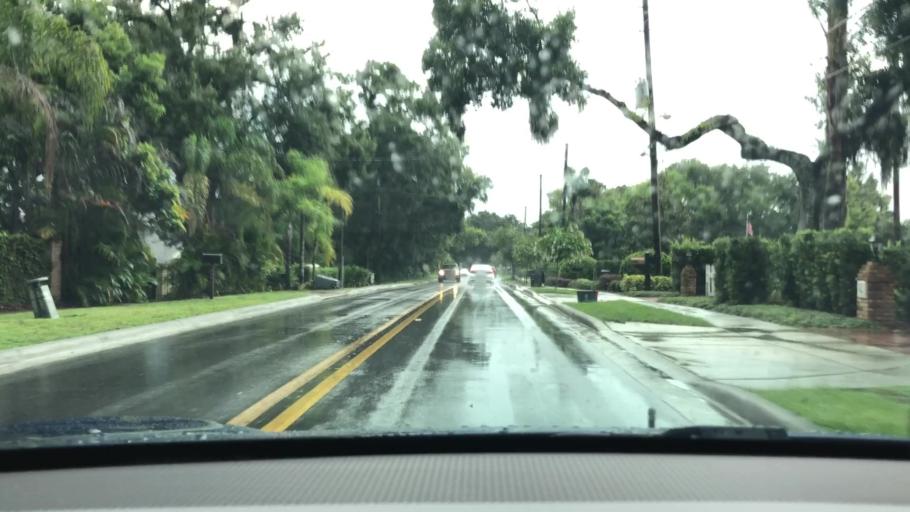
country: US
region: Florida
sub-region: Orange County
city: Edgewood
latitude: 28.4939
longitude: -81.3713
